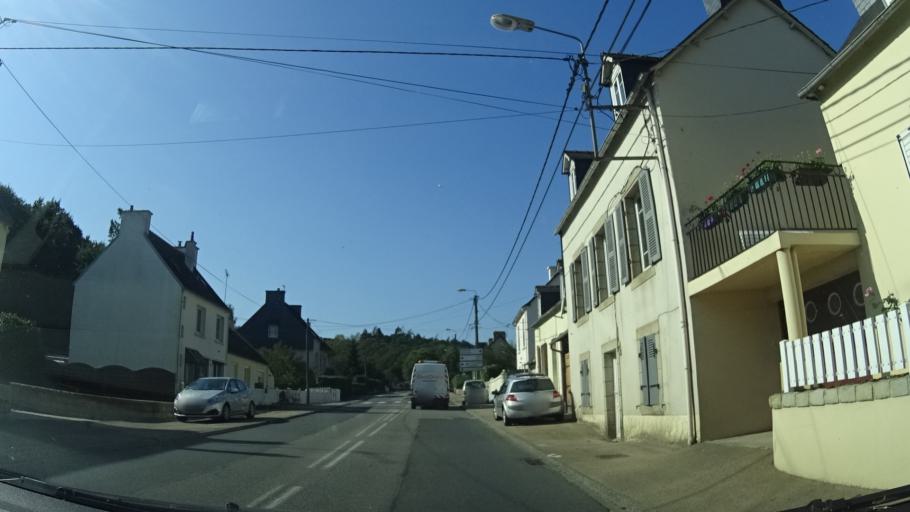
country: FR
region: Brittany
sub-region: Departement du Finistere
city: Chateaulin
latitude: 48.1935
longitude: -4.1073
